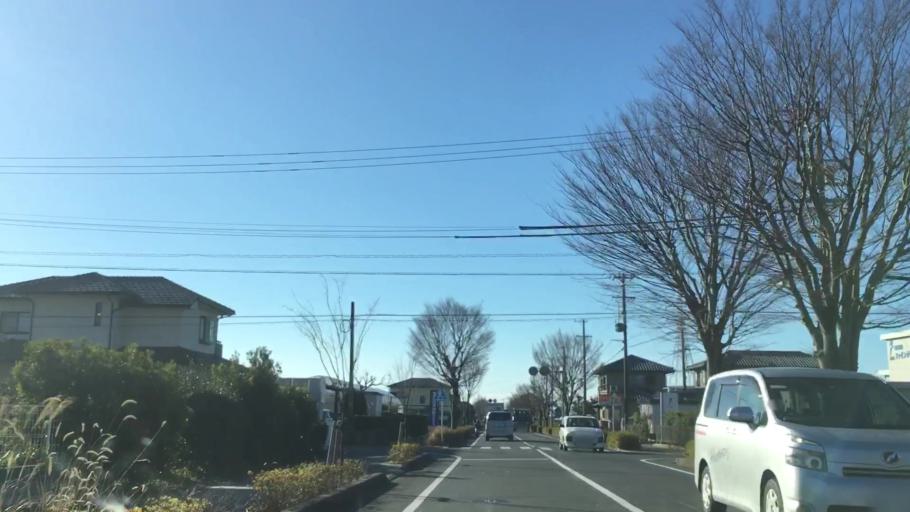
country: JP
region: Shizuoka
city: Hamakita
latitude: 34.8076
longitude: 137.7450
